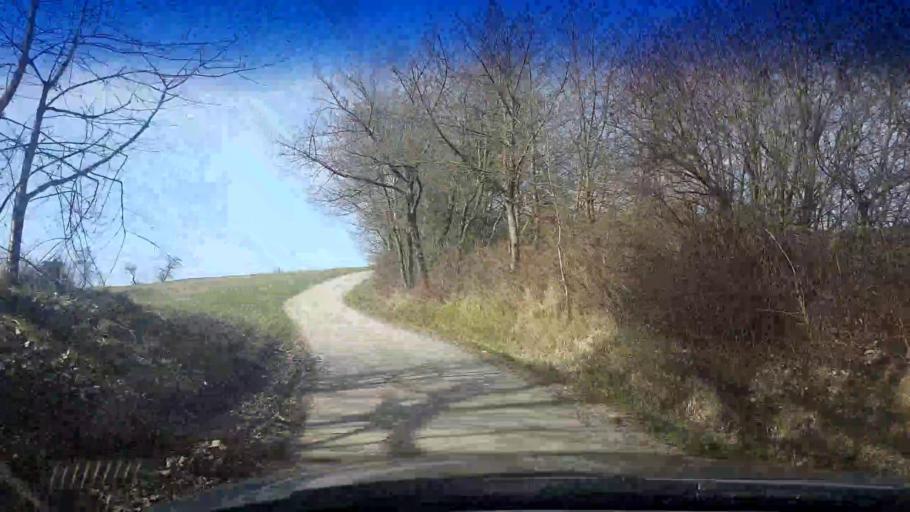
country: DE
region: Bavaria
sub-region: Upper Franconia
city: Bischberg
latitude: 49.8987
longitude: 10.8261
